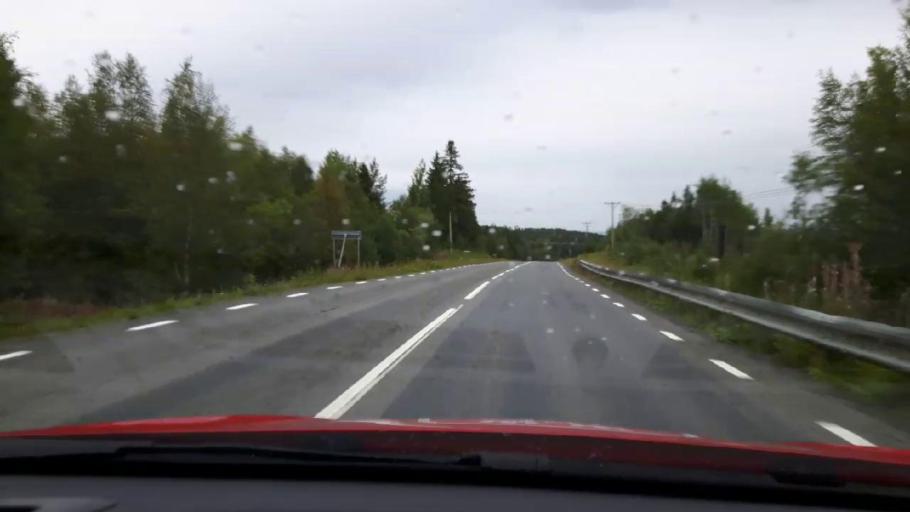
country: SE
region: Jaemtland
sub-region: Are Kommun
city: Jarpen
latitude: 63.3838
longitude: 13.4187
